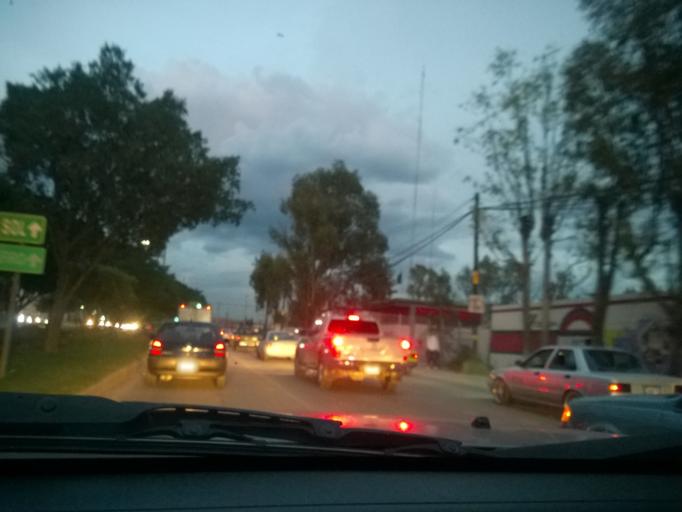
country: MX
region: Guanajuato
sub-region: Leon
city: Medina
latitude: 21.1253
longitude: -101.6315
